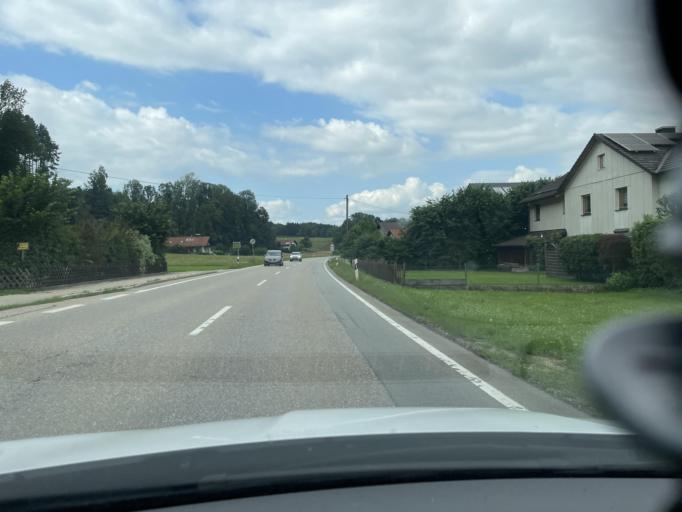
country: DE
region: Bavaria
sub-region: Upper Bavaria
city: Sankt Wolfgang
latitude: 48.2291
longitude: 12.1365
